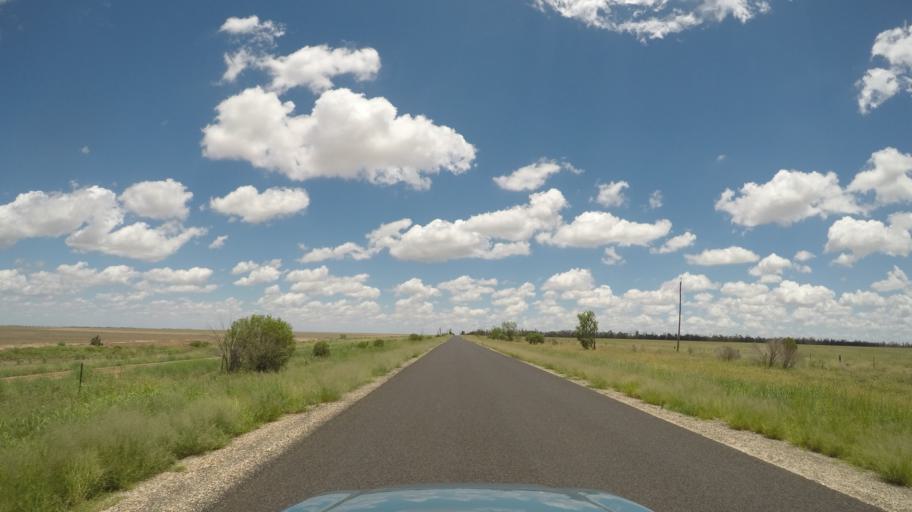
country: AU
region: Queensland
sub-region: Goondiwindi
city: Goondiwindi
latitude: -28.1643
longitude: 150.1641
